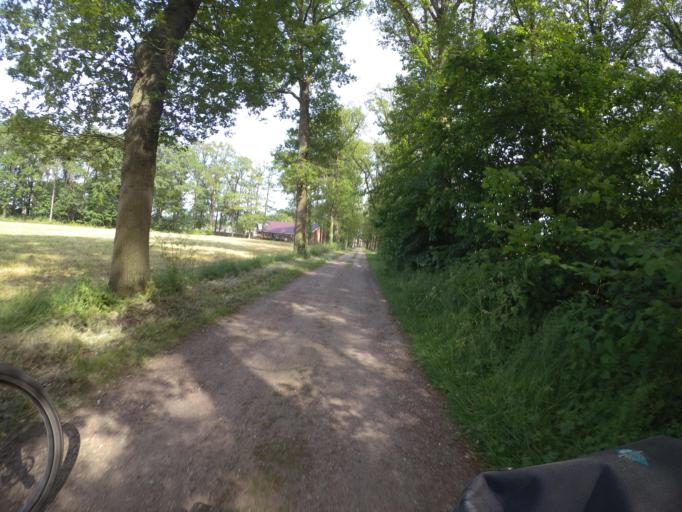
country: NL
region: Gelderland
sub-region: Gemeente Winterswijk
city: Winterswijk
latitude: 51.9306
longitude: 6.7122
